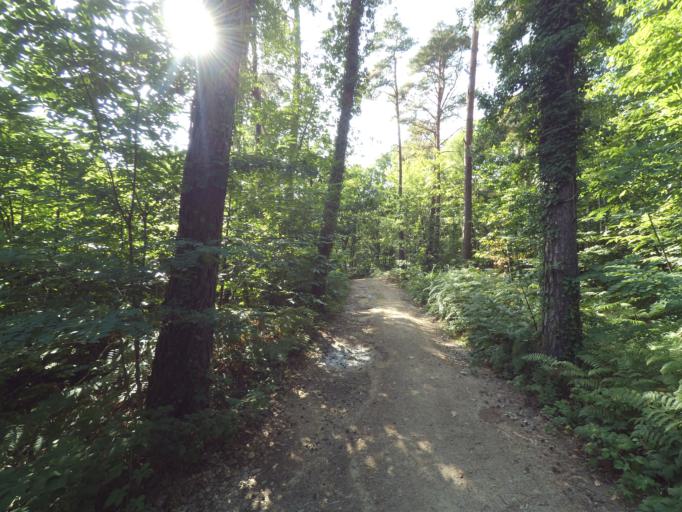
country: FR
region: Limousin
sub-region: Departement de la Haute-Vienne
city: Saint-Priest-sous-Aixe
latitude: 45.8205
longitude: 1.0607
